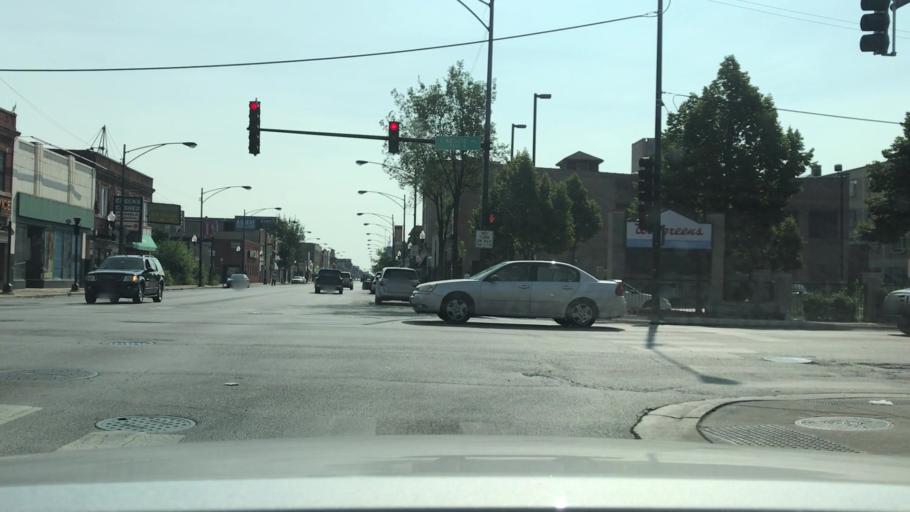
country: US
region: Illinois
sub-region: Cook County
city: Hometown
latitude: 41.7789
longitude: -87.7033
